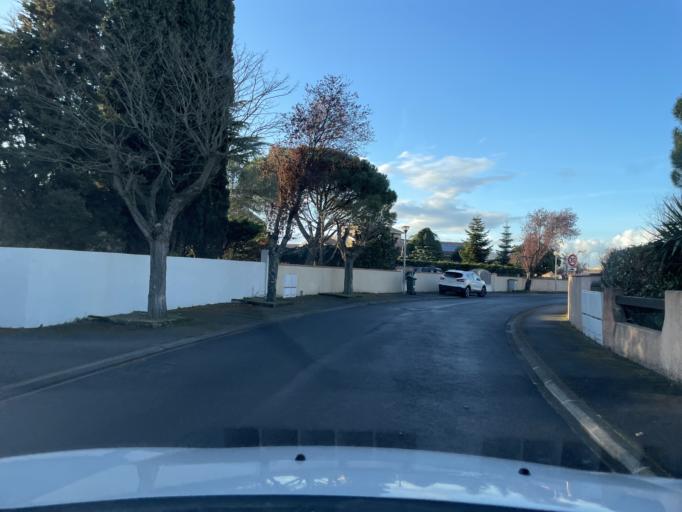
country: FR
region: Midi-Pyrenees
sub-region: Departement de la Haute-Garonne
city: Tournefeuille
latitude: 43.5916
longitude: 1.3269
